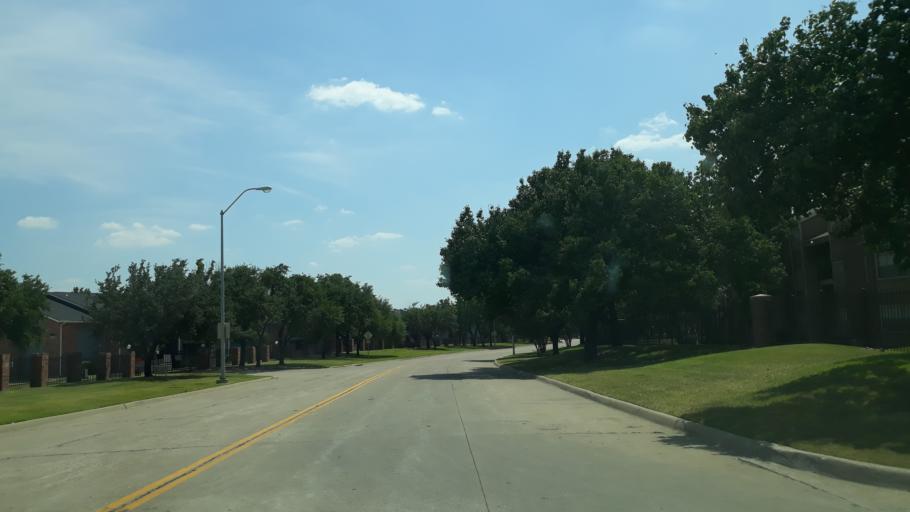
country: US
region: Texas
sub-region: Tarrant County
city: Euless
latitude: 32.8329
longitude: -97.0184
